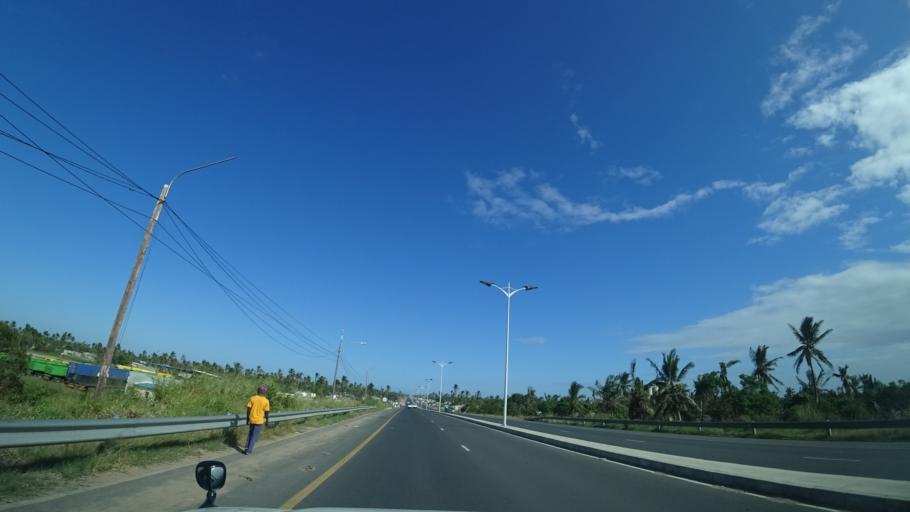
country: MZ
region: Sofala
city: Beira
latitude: -19.7390
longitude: 34.8519
